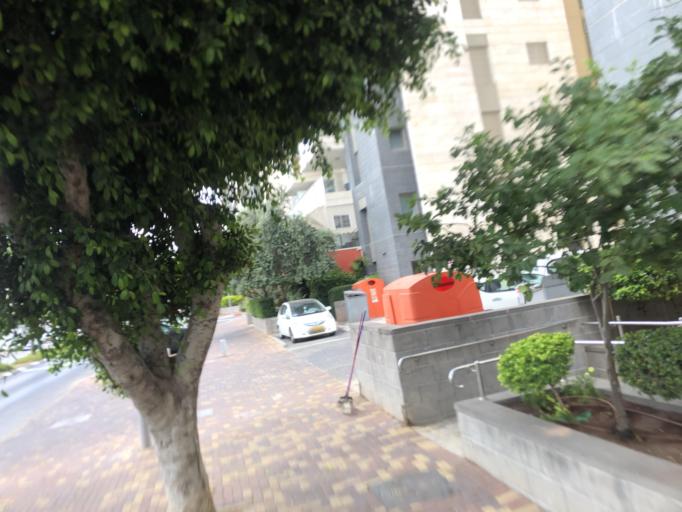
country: IL
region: Central District
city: Yehud
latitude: 32.0310
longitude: 34.8861
